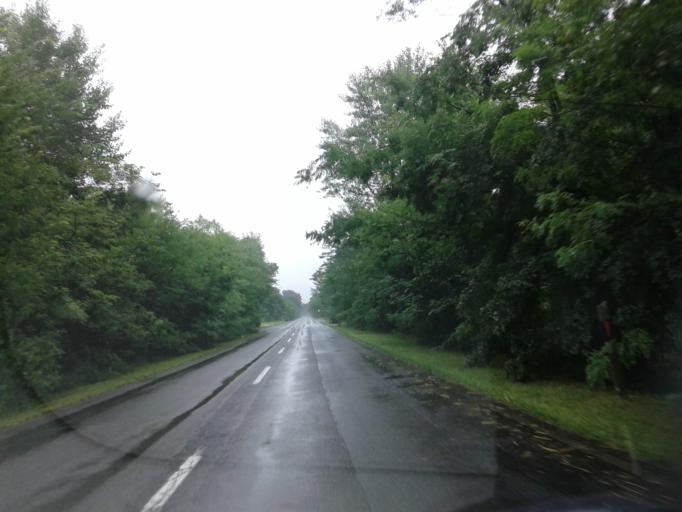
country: HU
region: Csongrad
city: Ruzsa
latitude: 46.2352
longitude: 19.7273
